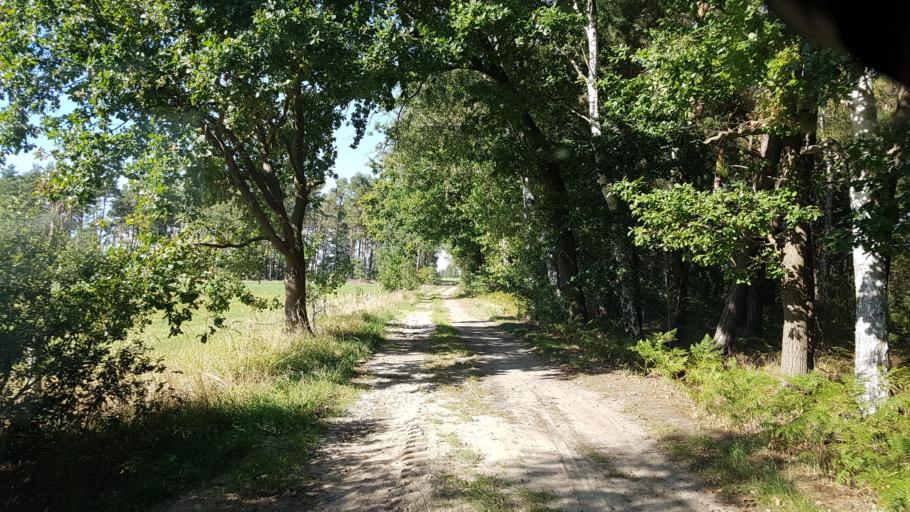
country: DE
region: Brandenburg
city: Ruckersdorf
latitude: 51.5496
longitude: 13.6076
